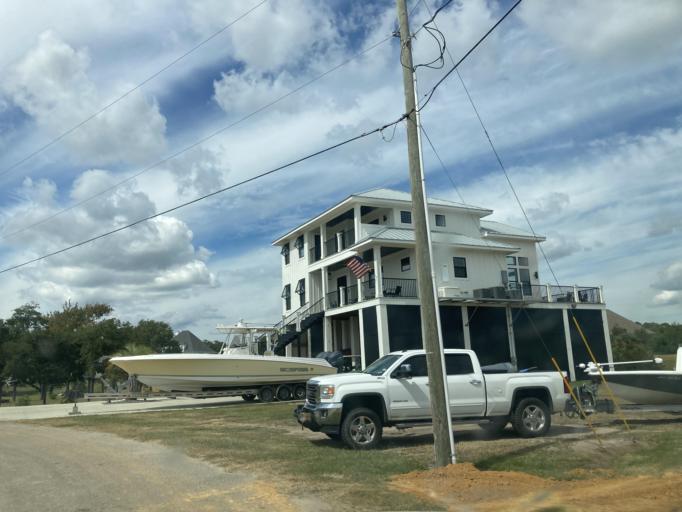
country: US
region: Mississippi
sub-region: Jackson County
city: Saint Martin
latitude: 30.4266
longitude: -88.8711
